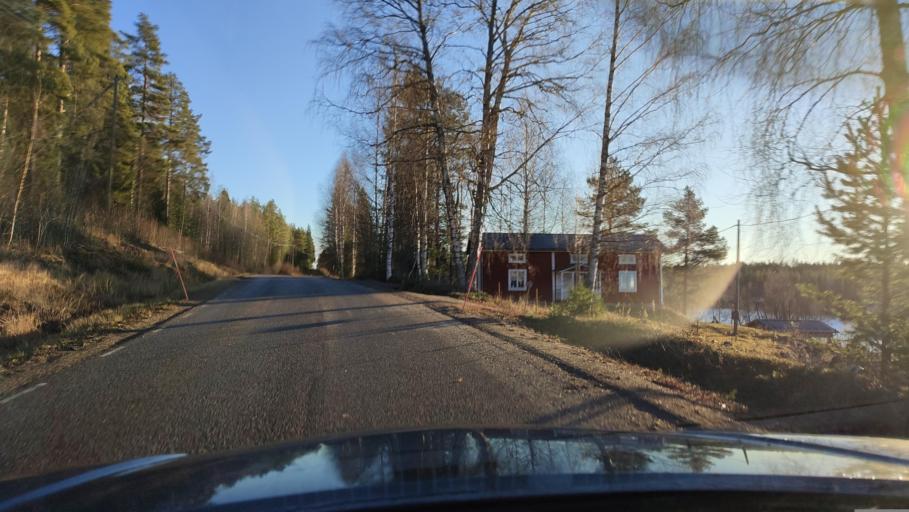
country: SE
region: Vaesterbotten
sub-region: Skelleftea Kommun
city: Viken
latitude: 64.6978
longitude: 20.9138
